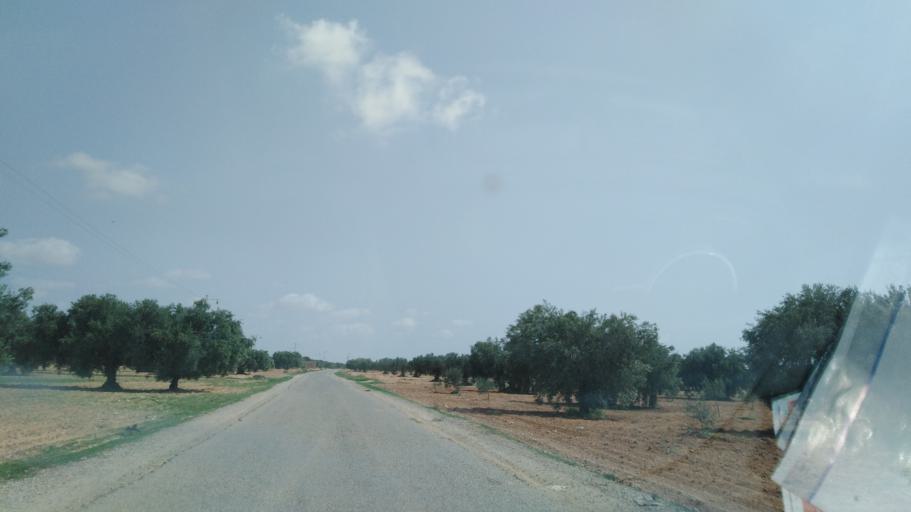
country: TN
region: Safaqis
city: Sfax
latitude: 34.6333
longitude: 10.6049
